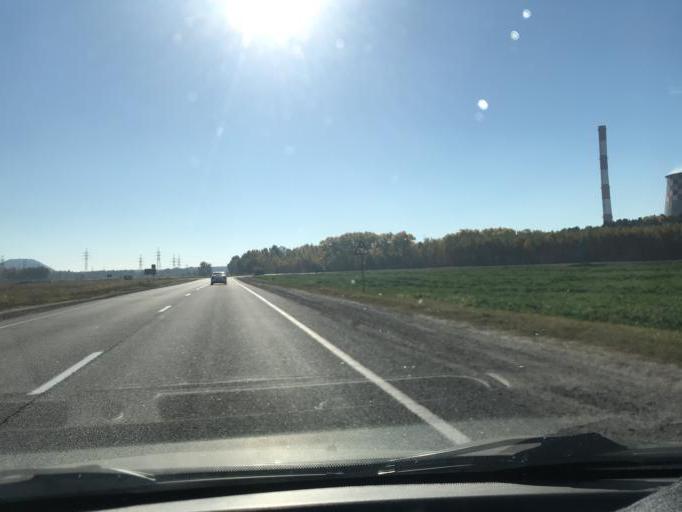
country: BY
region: Gomel
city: Kastsyukowka
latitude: 52.4556
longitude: 30.8248
